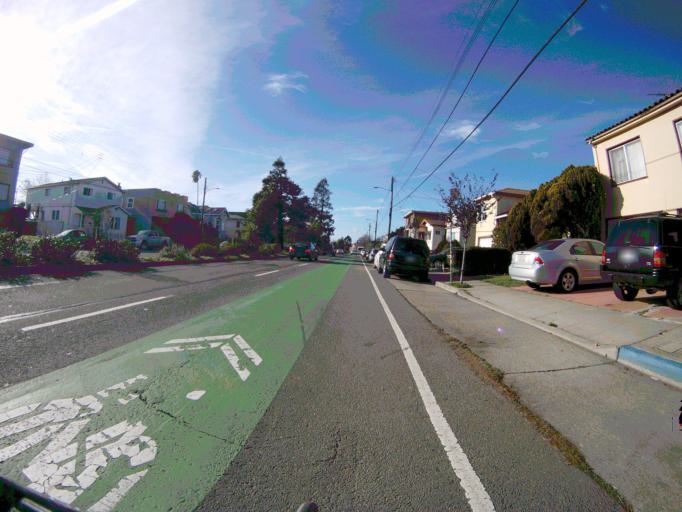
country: US
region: California
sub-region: Alameda County
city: Emeryville
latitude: 37.8304
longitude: -122.2723
